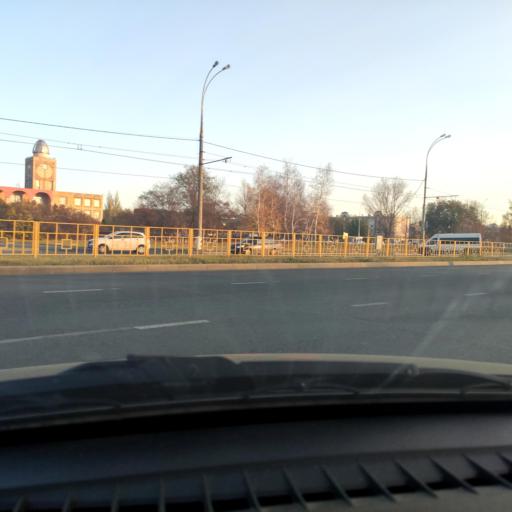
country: RU
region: Samara
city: Tol'yatti
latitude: 53.4998
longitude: 49.2899
